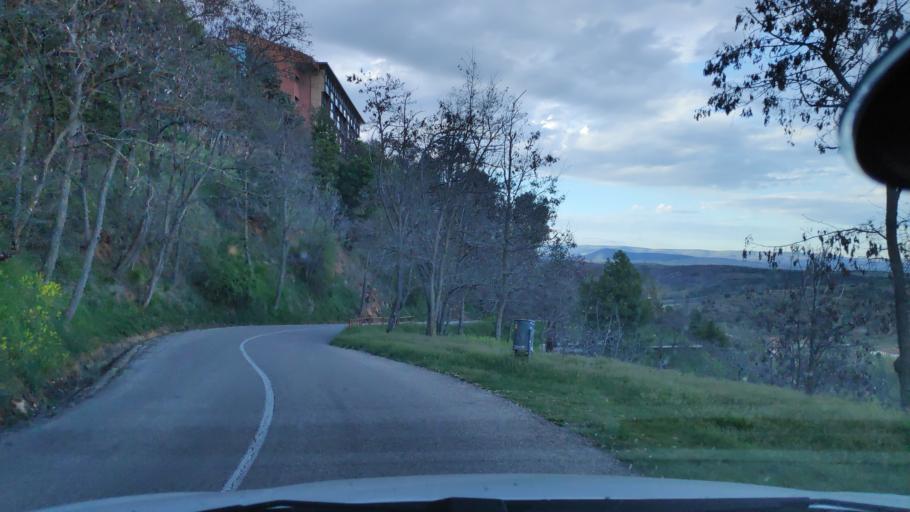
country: ES
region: Castille and Leon
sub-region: Provincia de Soria
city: Soria
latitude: 41.7614
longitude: -2.4570
